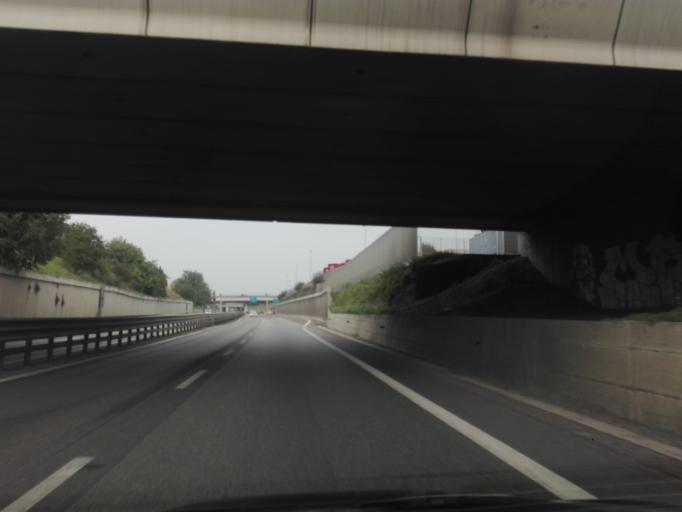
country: IT
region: Veneto
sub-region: Provincia di Verona
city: San Giovanni Lupatoto
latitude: 45.3962
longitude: 11.0159
